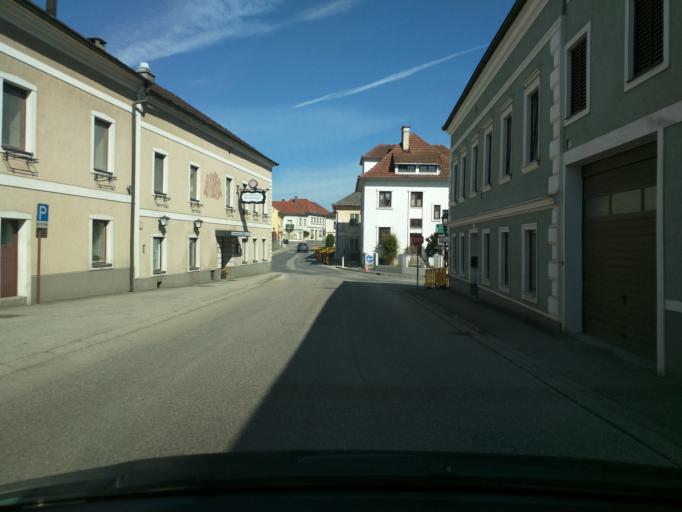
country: AT
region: Lower Austria
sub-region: Politischer Bezirk Amstetten
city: Euratsfeld
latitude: 48.0809
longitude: 14.9328
